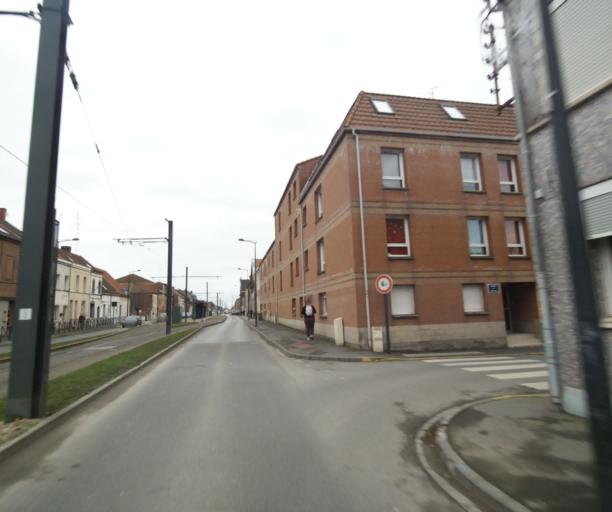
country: FR
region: Nord-Pas-de-Calais
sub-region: Departement du Nord
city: Bruay-sur-l'Escaut
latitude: 50.3917
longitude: 3.5318
